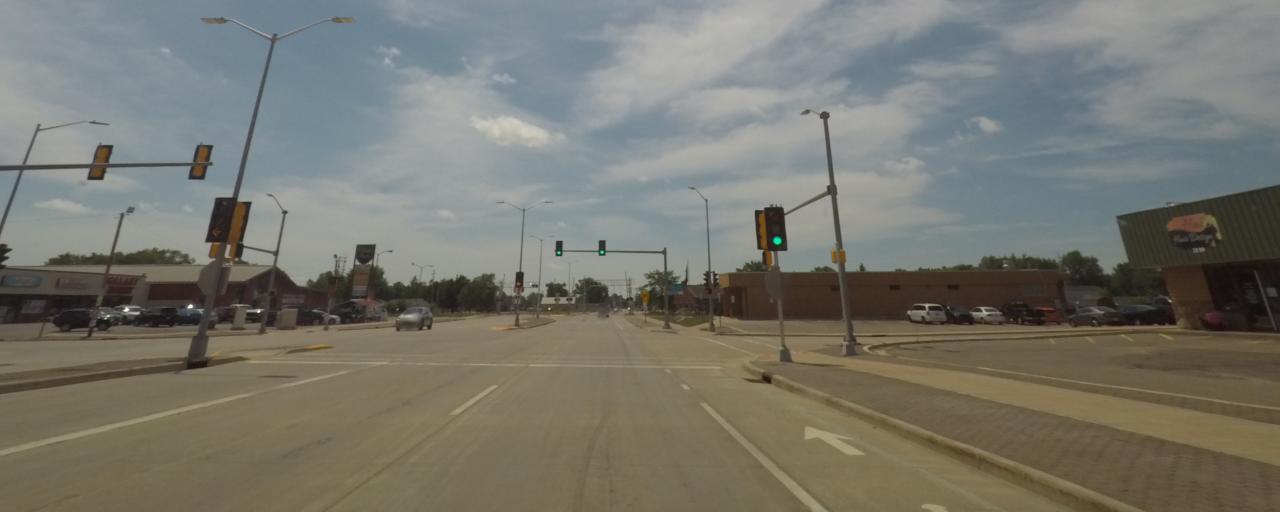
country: US
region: Wisconsin
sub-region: Portage County
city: Plover
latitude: 44.4585
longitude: -89.5437
